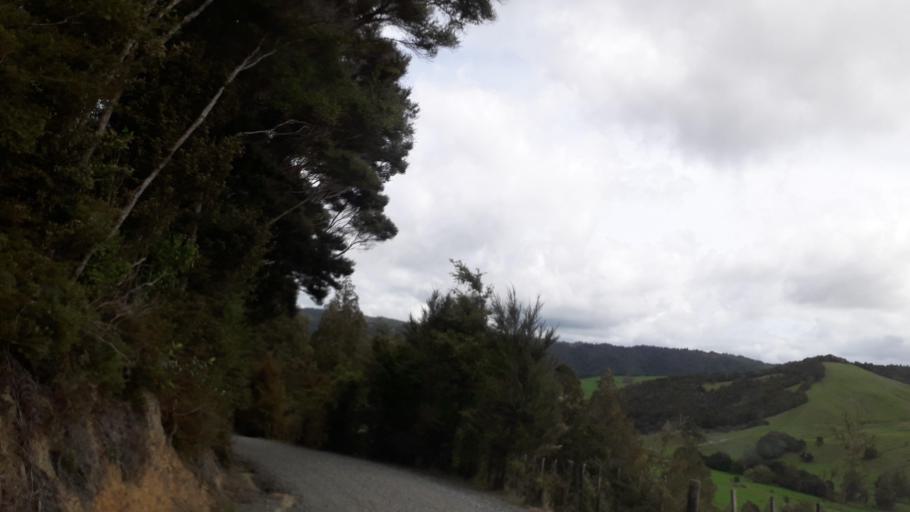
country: NZ
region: Northland
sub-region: Far North District
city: Waimate North
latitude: -35.1421
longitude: 173.7141
